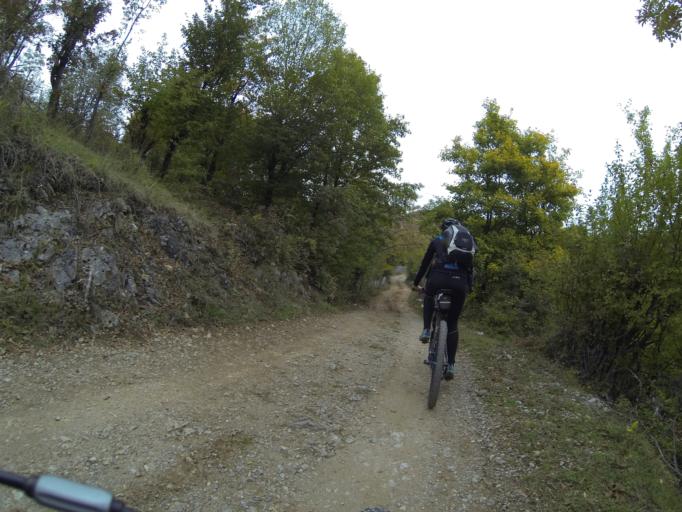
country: RO
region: Gorj
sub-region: Comuna Tismana
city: Sohodol
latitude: 45.0655
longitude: 22.8681
